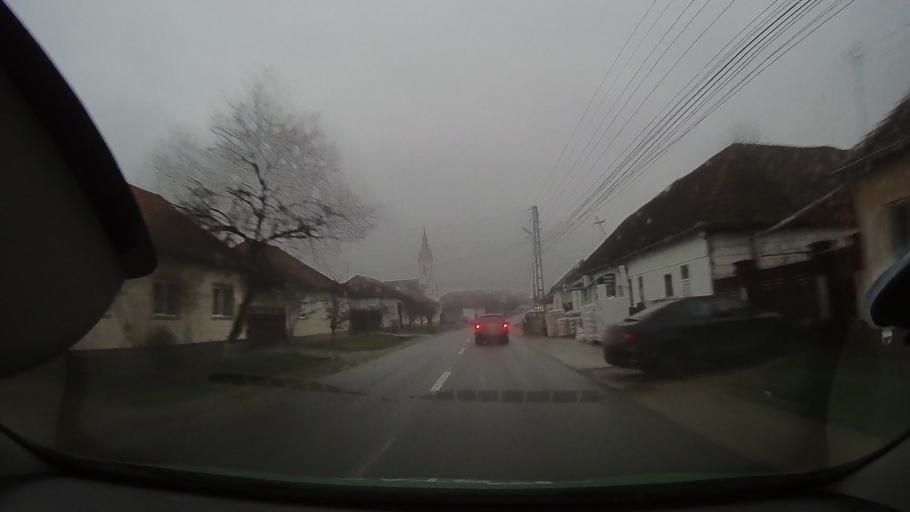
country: RO
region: Arad
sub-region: Comuna Craiova
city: Craiova
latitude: 46.5838
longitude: 21.9734
